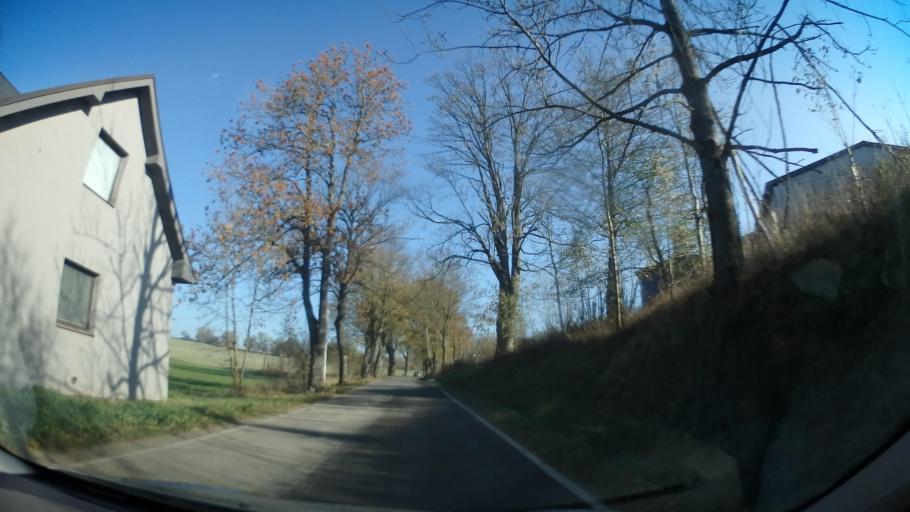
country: CZ
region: Vysocina
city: Zd'ar nad Sazavou Druhy
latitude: 49.6094
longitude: 15.9185
